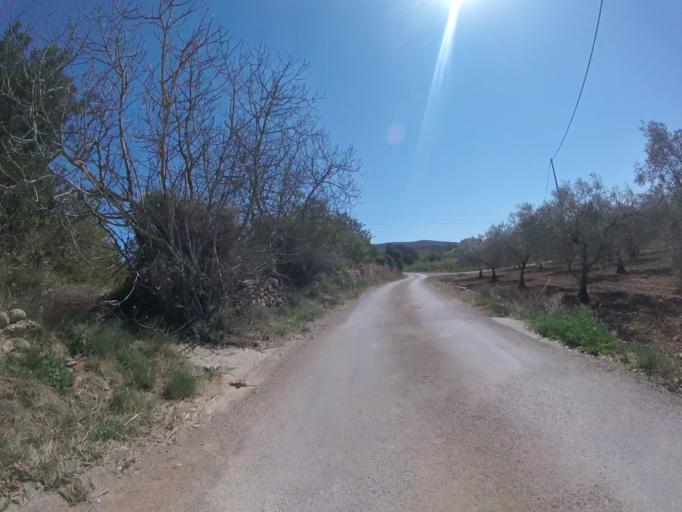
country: ES
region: Valencia
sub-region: Provincia de Castello
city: Cuevas de Vinroma
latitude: 40.3745
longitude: 0.1344
